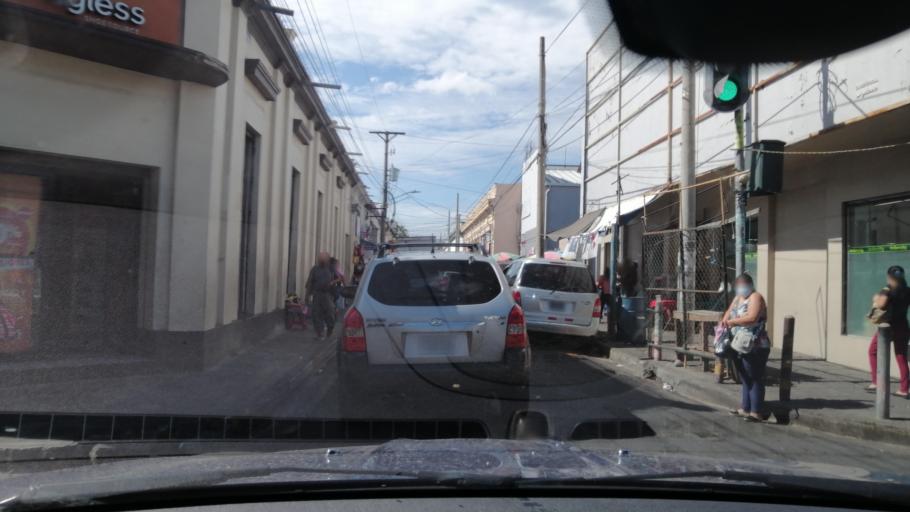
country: SV
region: Santa Ana
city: Santa Ana
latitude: 13.9937
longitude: -89.5589
